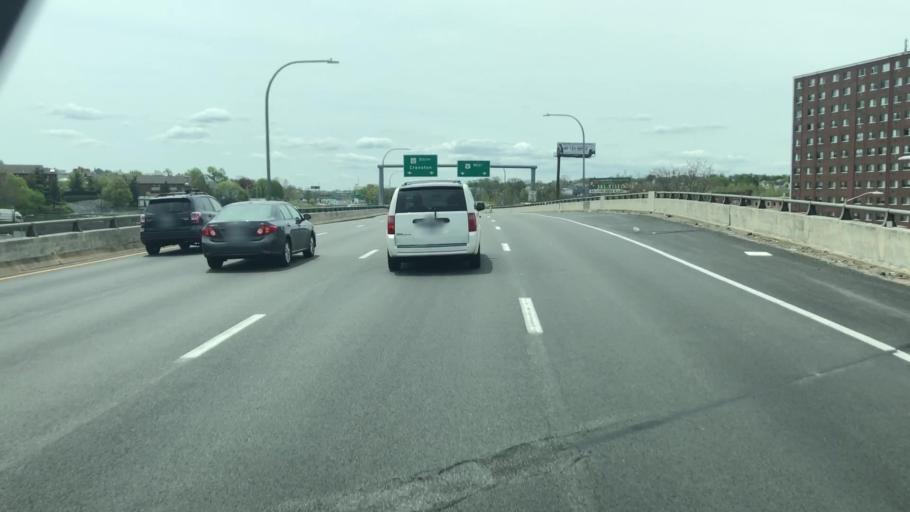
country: US
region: Rhode Island
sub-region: Providence County
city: Providence
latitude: 41.8176
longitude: -71.4390
